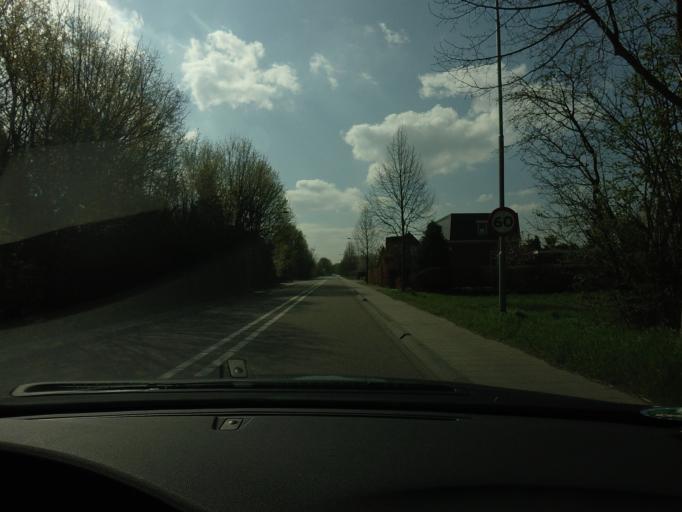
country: NL
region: Limburg
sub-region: Eijsden-Margraten
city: Eijsden
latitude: 50.7947
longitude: 5.7294
